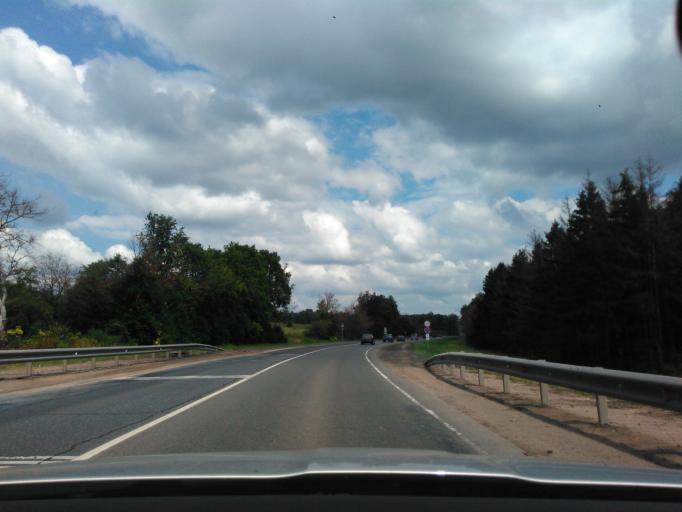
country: RU
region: Moskovskaya
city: Radumlya
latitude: 56.1079
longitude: 37.1892
